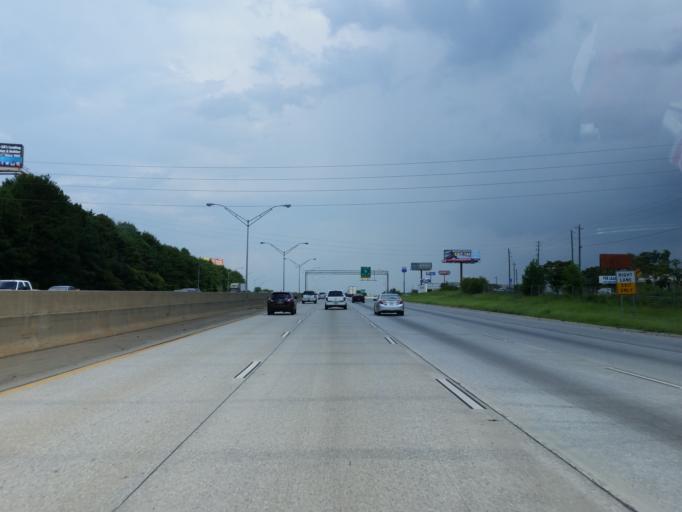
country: US
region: Georgia
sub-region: Monroe County
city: Forsyth
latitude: 33.0318
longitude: -83.9163
